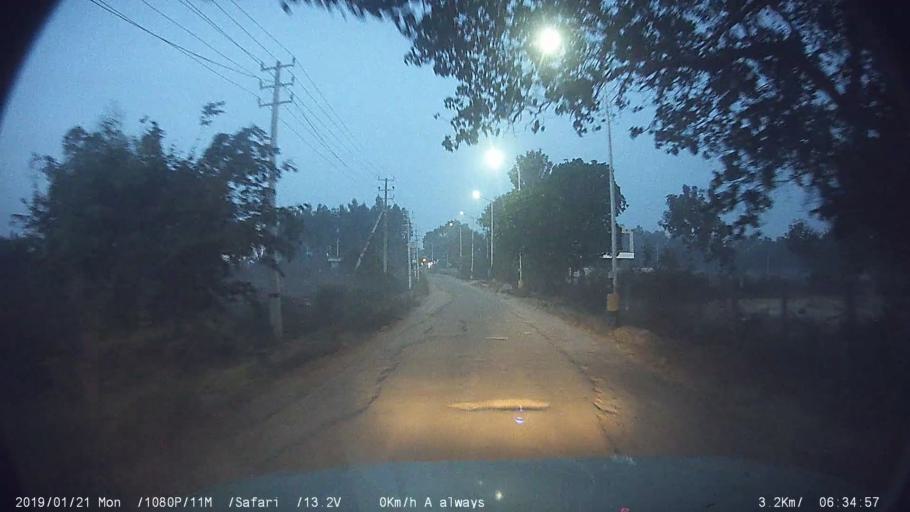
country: IN
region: Karnataka
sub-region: Bangalore Urban
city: Anekal
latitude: 12.8259
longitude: 77.6346
